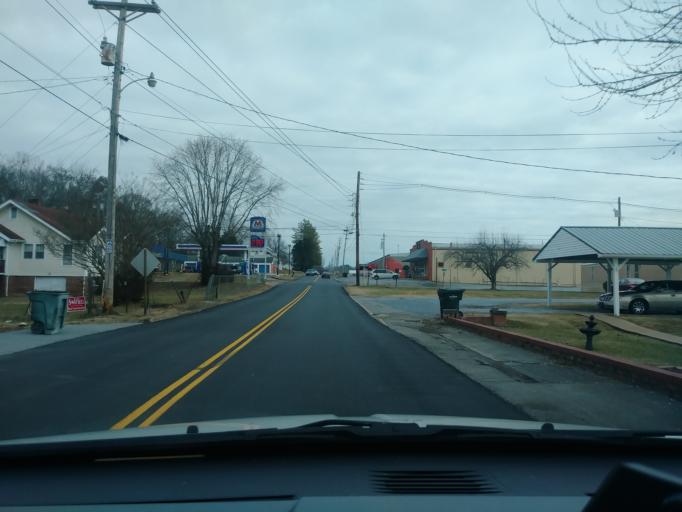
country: US
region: Tennessee
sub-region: Greene County
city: Greeneville
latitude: 36.1575
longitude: -82.8264
